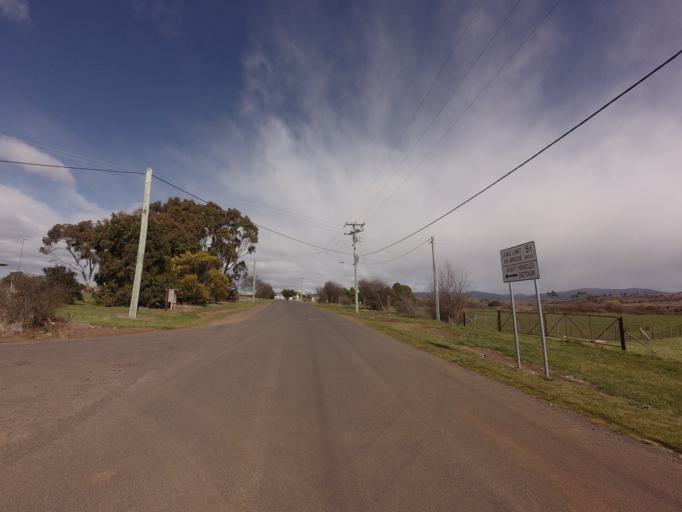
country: AU
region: Tasmania
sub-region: Northern Midlands
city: Evandale
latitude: -42.1339
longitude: 147.4282
